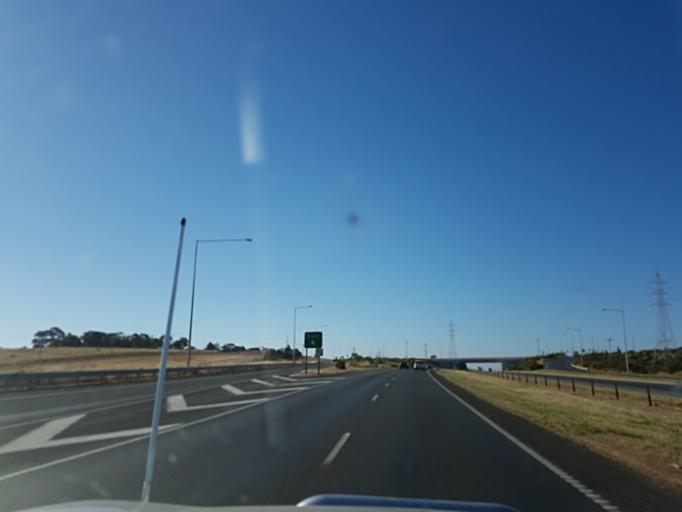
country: AU
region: Victoria
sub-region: Greater Geelong
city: Wandana Heights
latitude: -38.1753
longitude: 144.2936
